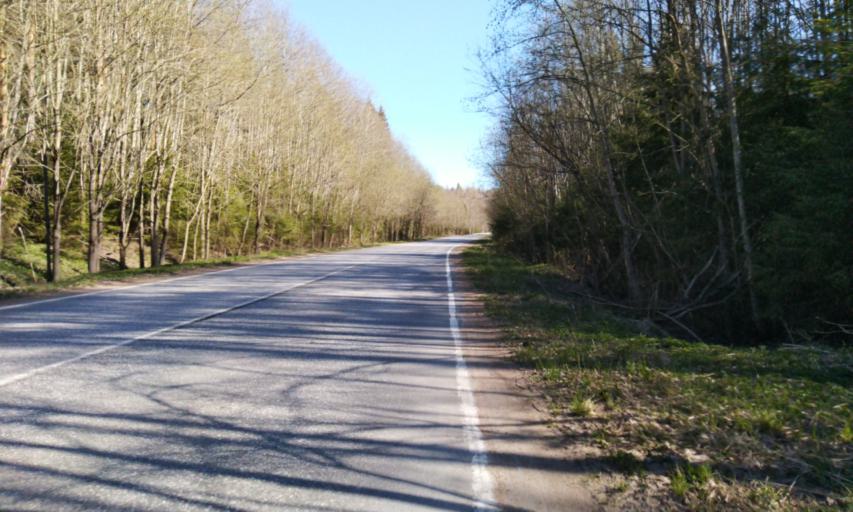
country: RU
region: Leningrad
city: Garbolovo
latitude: 60.3691
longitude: 30.4408
